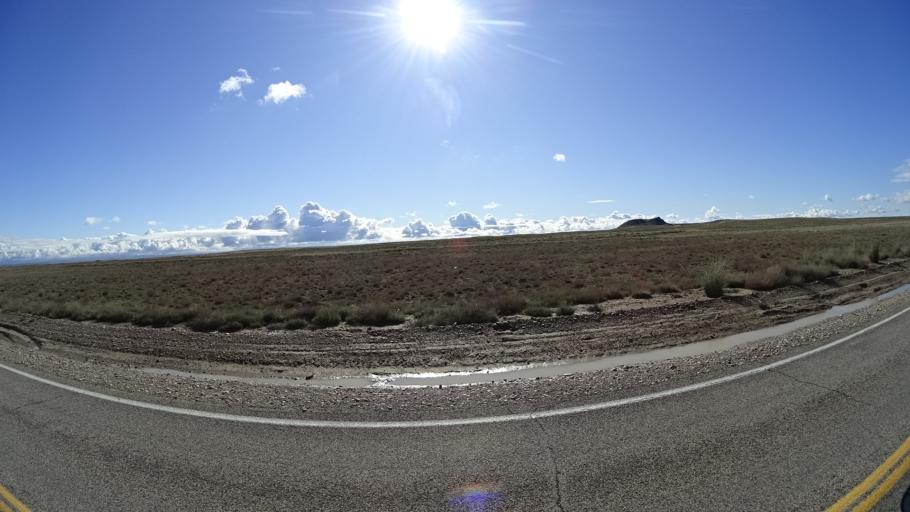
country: US
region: Idaho
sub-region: Ada County
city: Kuna
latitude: 43.3803
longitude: -116.4139
